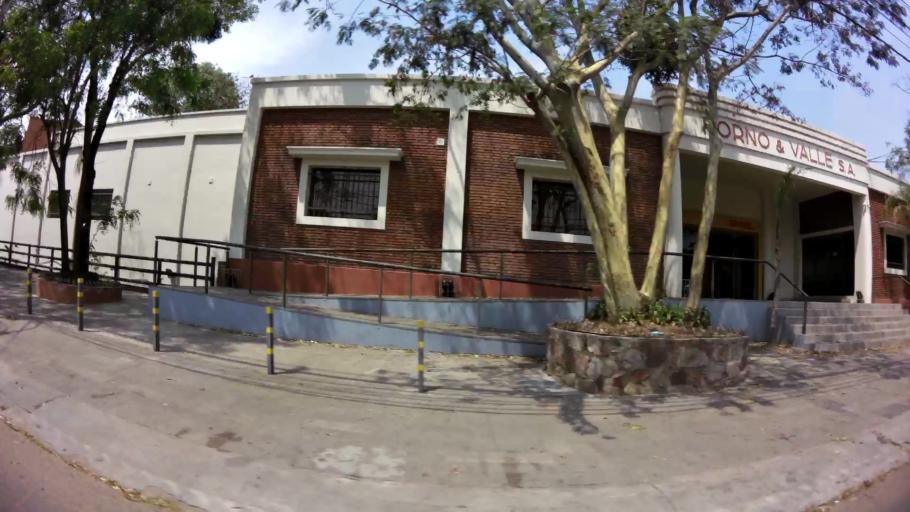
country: PY
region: Asuncion
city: Asuncion
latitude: -25.2789
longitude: -57.6096
